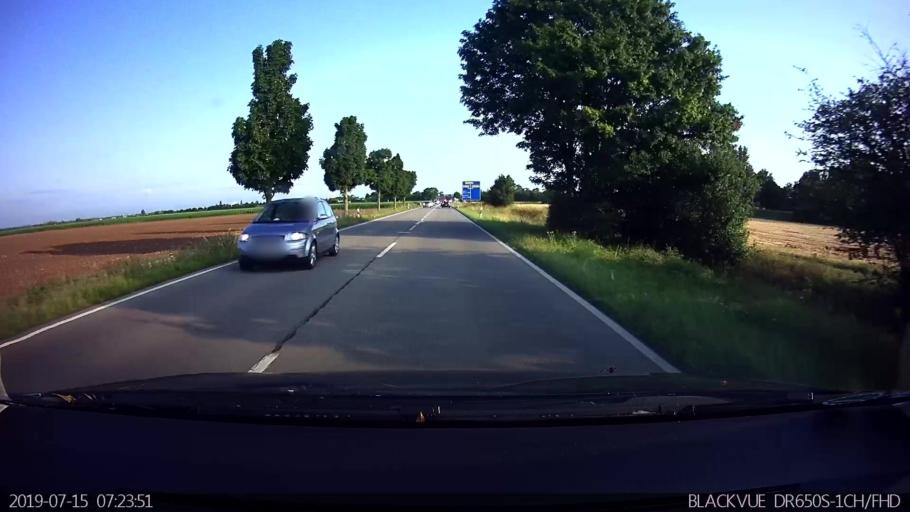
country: DE
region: Baden-Wuerttemberg
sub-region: Freiburg Region
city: Unterkrozingen
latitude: 47.9475
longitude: 7.6734
